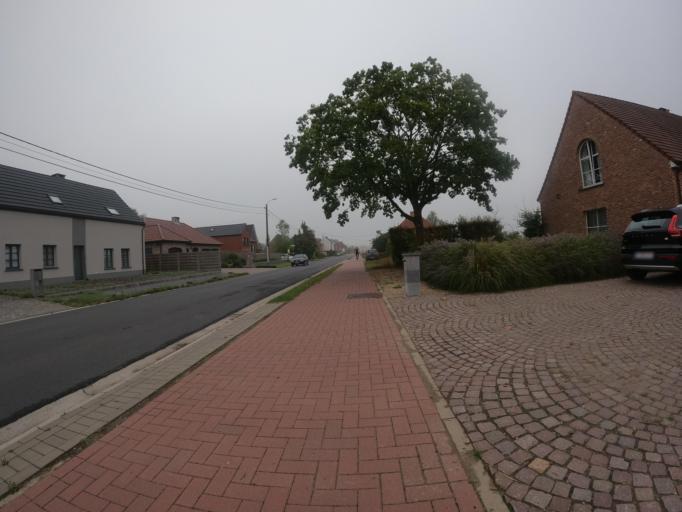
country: BE
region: Flanders
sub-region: Provincie Antwerpen
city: Putte
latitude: 51.0595
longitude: 4.5961
